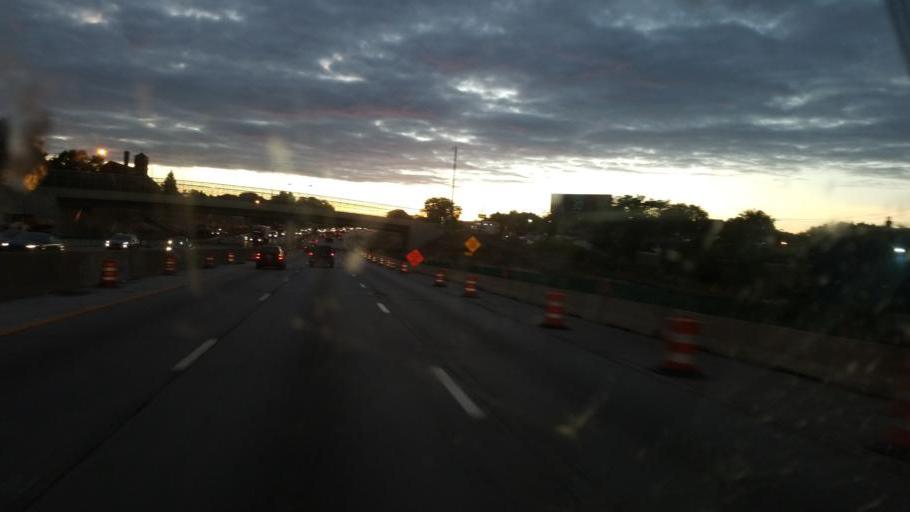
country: US
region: Ohio
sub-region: Summit County
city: Akron
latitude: 41.0624
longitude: -81.5217
